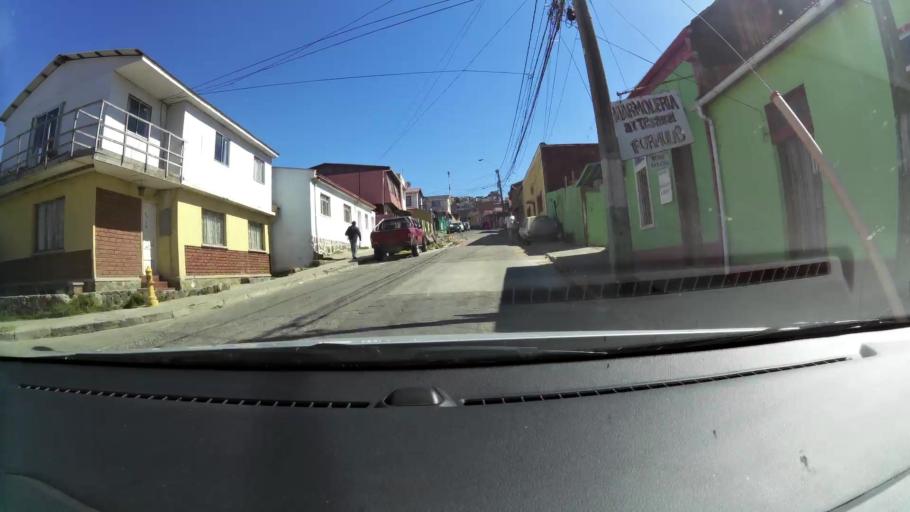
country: CL
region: Valparaiso
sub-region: Provincia de Valparaiso
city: Valparaiso
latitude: -33.0251
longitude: -71.6432
